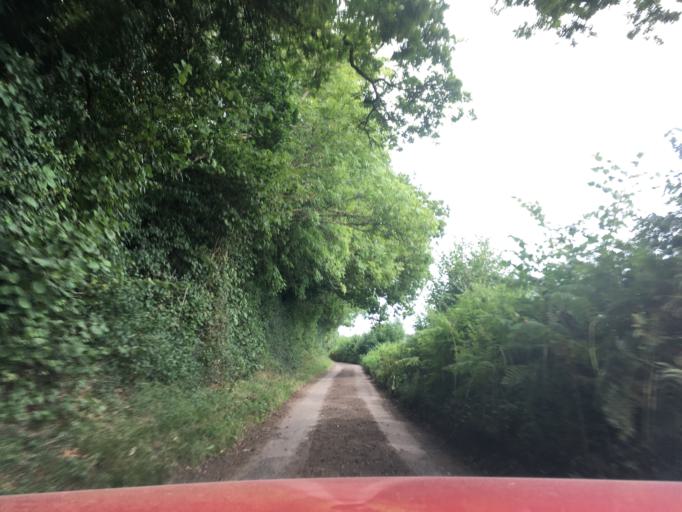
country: GB
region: England
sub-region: South Gloucestershire
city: Tytherington
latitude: 51.6082
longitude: -2.4576
